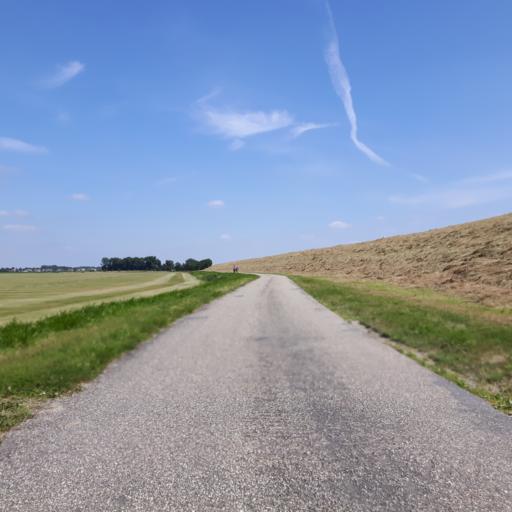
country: NL
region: Zeeland
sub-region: Schouwen-Duiveland
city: Bruinisse
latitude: 51.6133
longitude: 4.1355
